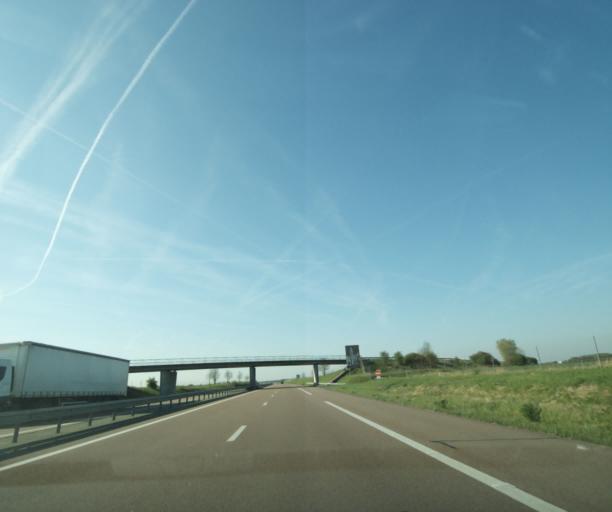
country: FR
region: Ile-de-France
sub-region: Departement de Seine-et-Marne
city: Souppes-sur-Loing
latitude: 48.1985
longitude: 2.7699
